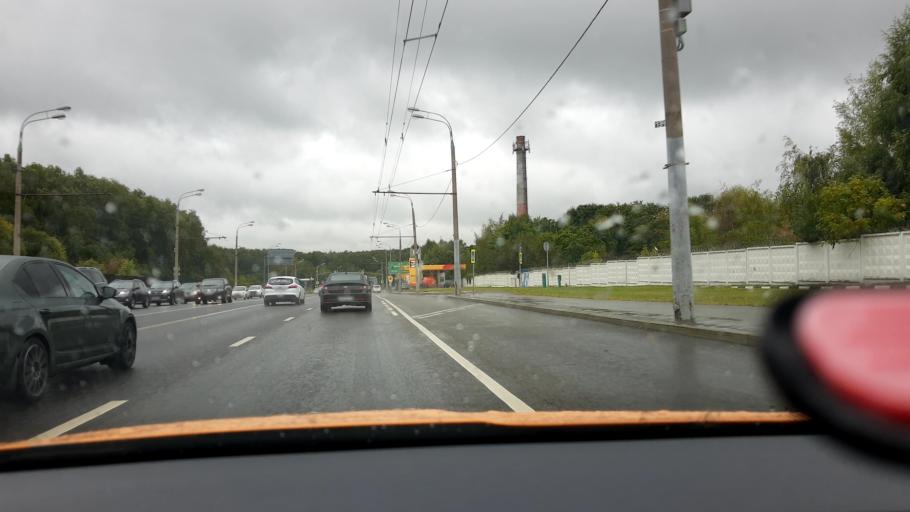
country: RU
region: Moscow
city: Zyuzino
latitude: 55.6479
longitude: 37.5622
